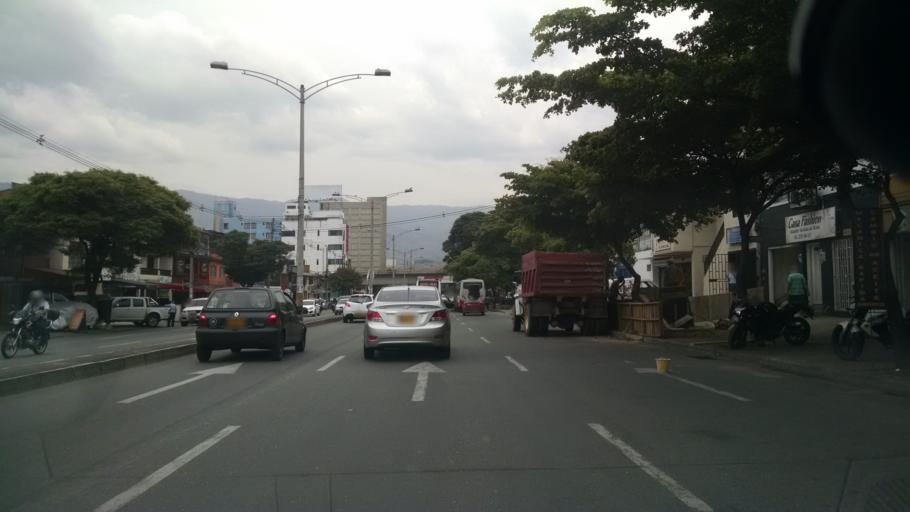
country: CO
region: Antioquia
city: Medellin
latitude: 6.2393
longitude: -75.5845
